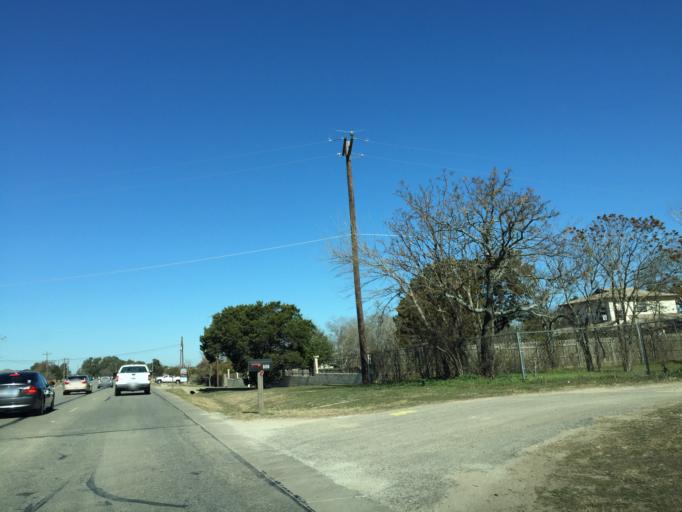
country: US
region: Texas
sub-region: Williamson County
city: Leander
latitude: 30.5632
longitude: -97.8634
